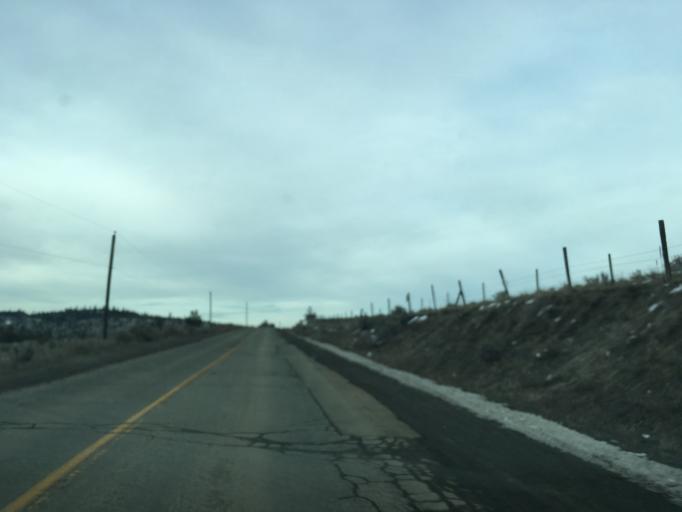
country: CA
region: British Columbia
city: Kamloops
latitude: 50.6214
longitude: -120.4429
